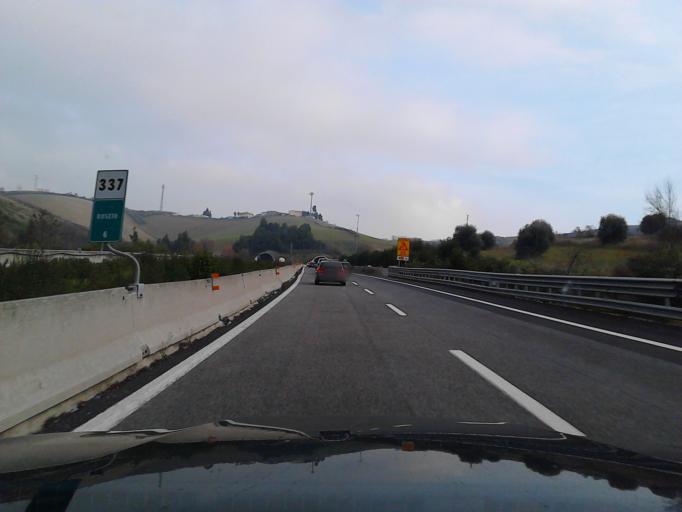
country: IT
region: Abruzzo
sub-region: Provincia di Teramo
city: Morro d'Oro
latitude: 42.6916
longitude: 13.9293
